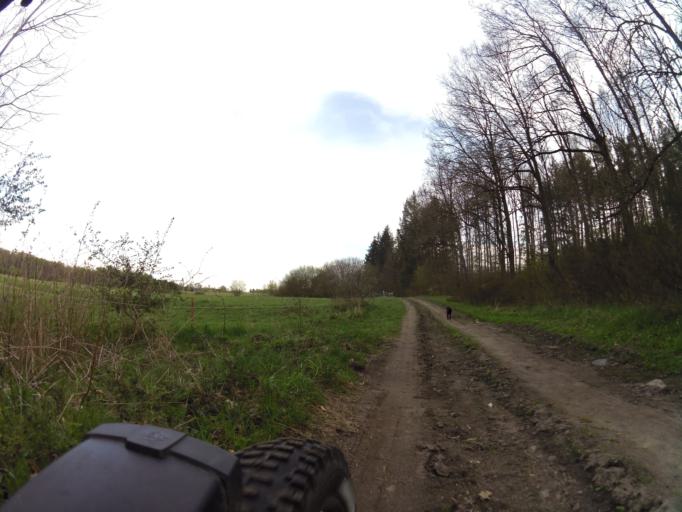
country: PL
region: West Pomeranian Voivodeship
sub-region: Powiat lobeski
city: Lobez
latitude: 53.7383
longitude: 15.6324
